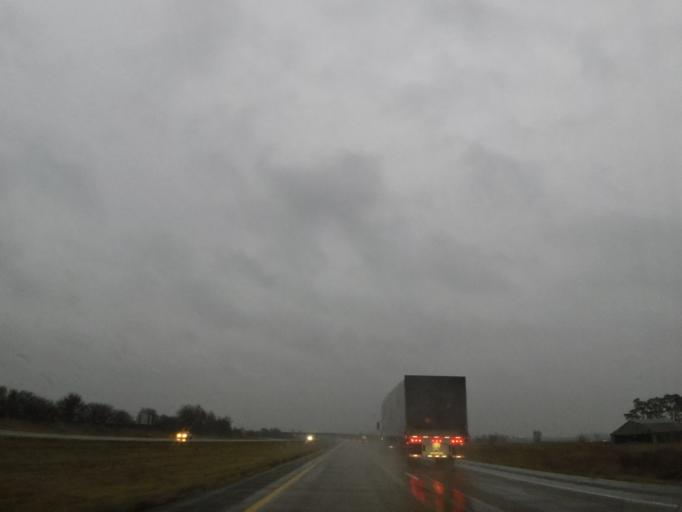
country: US
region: Iowa
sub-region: Cerro Gordo County
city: Clear Lake
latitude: 43.1927
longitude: -93.3524
